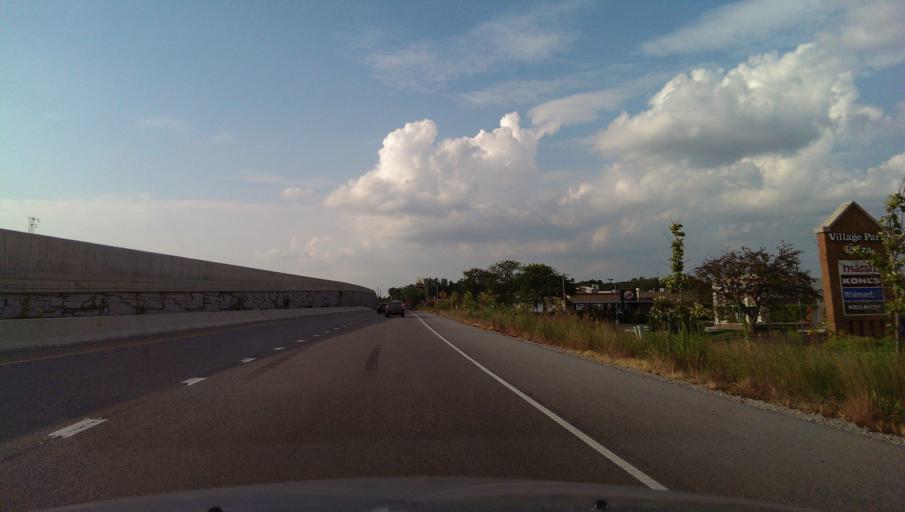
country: US
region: Indiana
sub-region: Hamilton County
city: Carmel
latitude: 40.0045
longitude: -86.1270
